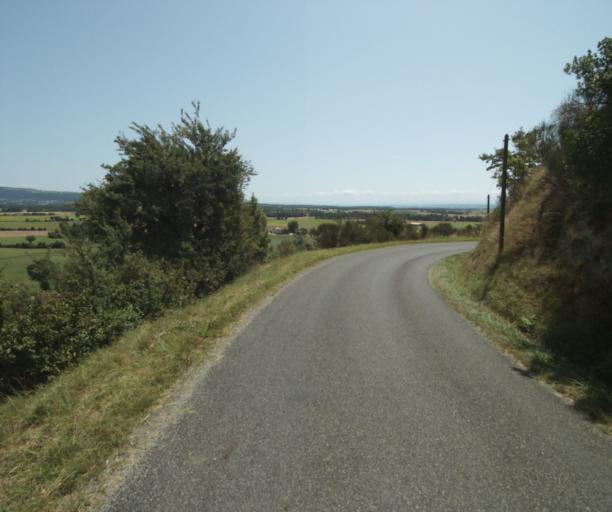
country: FR
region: Midi-Pyrenees
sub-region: Departement de la Haute-Garonne
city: Saint-Felix-Lauragais
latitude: 43.4392
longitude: 1.8964
